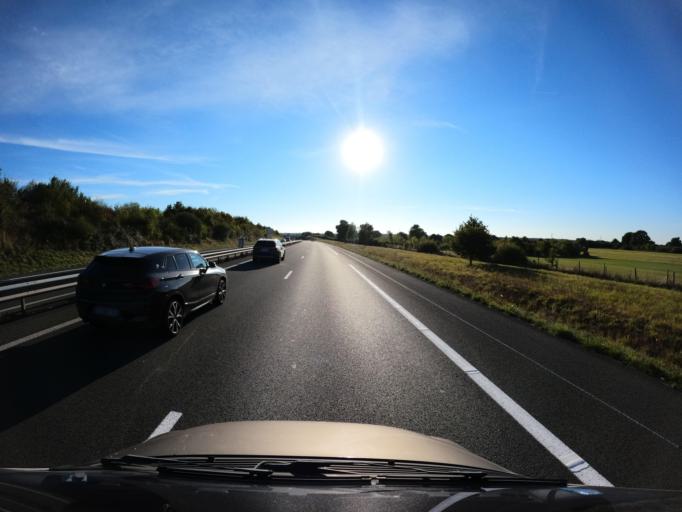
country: FR
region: Pays de la Loire
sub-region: Departement de Maine-et-Loire
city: Chemille-Melay
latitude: 47.2347
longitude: -0.7452
